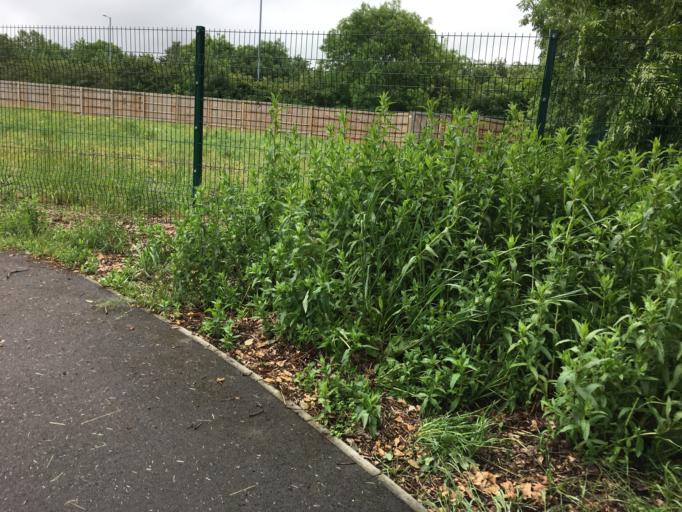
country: GB
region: England
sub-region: Warwickshire
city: Rugby
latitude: 52.3972
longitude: -1.2489
